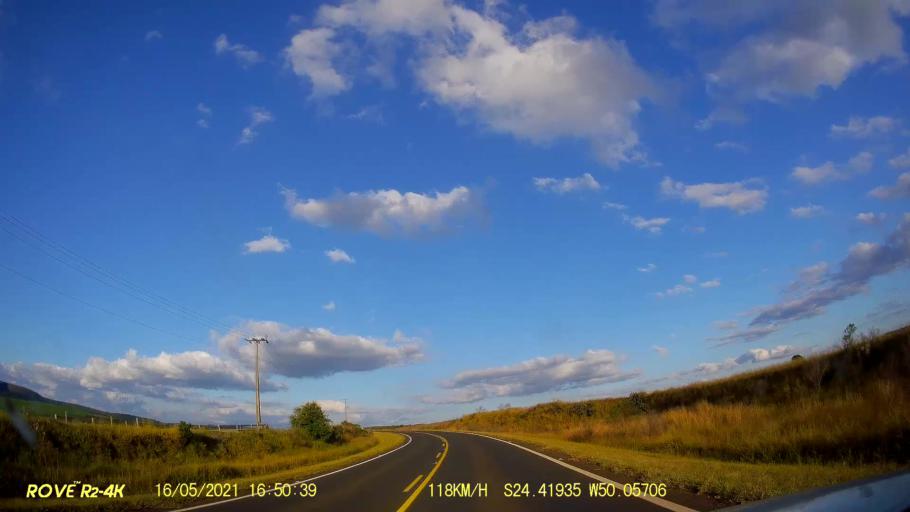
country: BR
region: Parana
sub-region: Pirai Do Sul
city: Pirai do Sul
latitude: -24.4197
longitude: -50.0572
